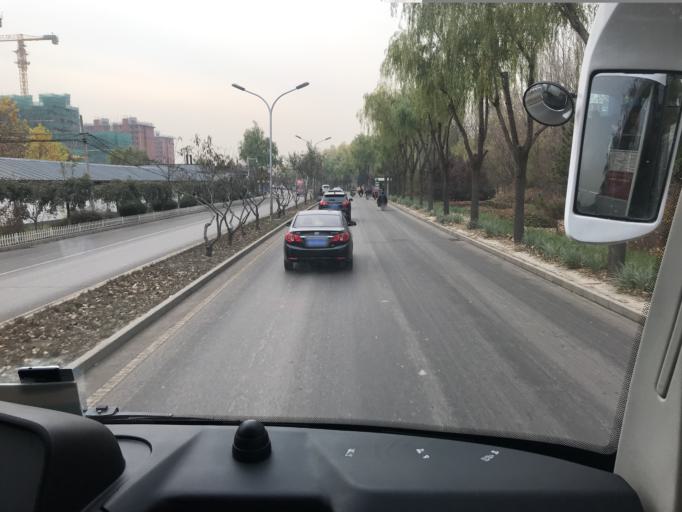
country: CN
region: Beijing
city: Sujiatuo
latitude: 40.0956
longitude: 116.2083
